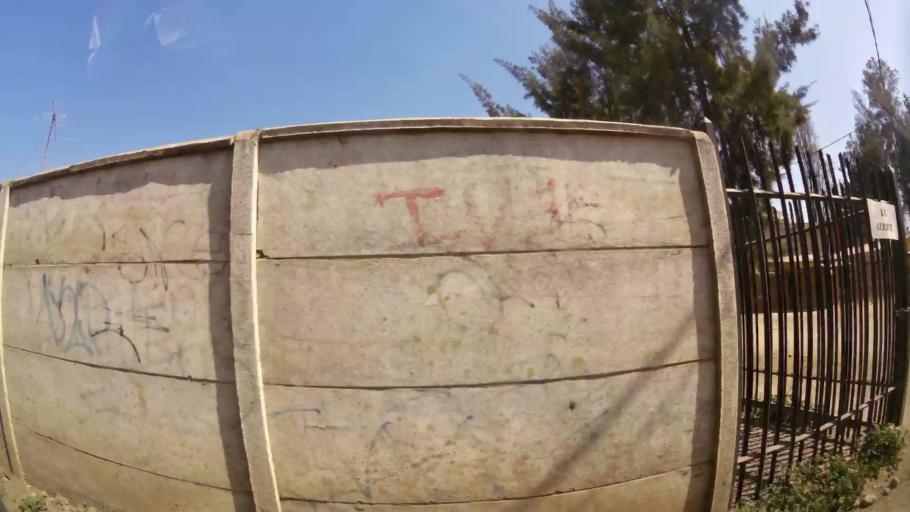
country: CL
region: Santiago Metropolitan
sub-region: Provincia de Talagante
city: Penaflor
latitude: -33.5854
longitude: -70.8114
